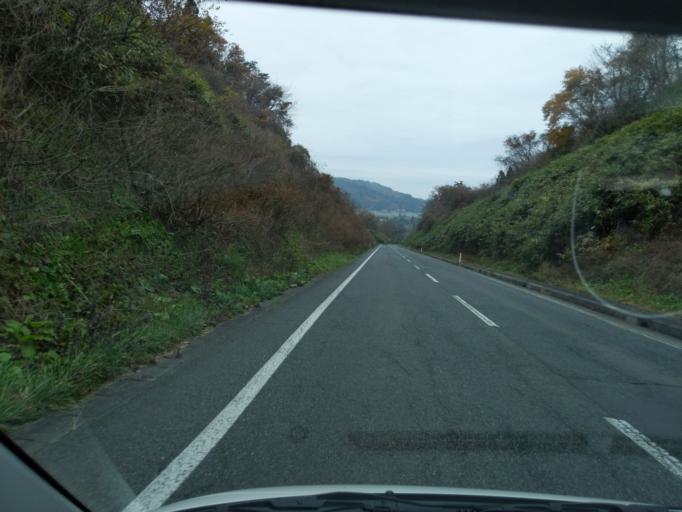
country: JP
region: Iwate
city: Mizusawa
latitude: 39.2080
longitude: 141.2200
